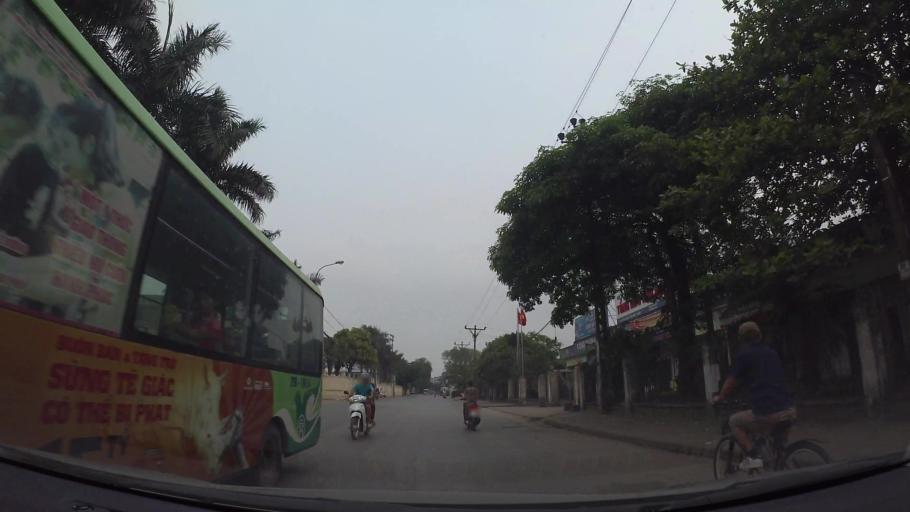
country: VN
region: Ha Noi
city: Hoan Kiem
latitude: 21.0663
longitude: 105.8921
